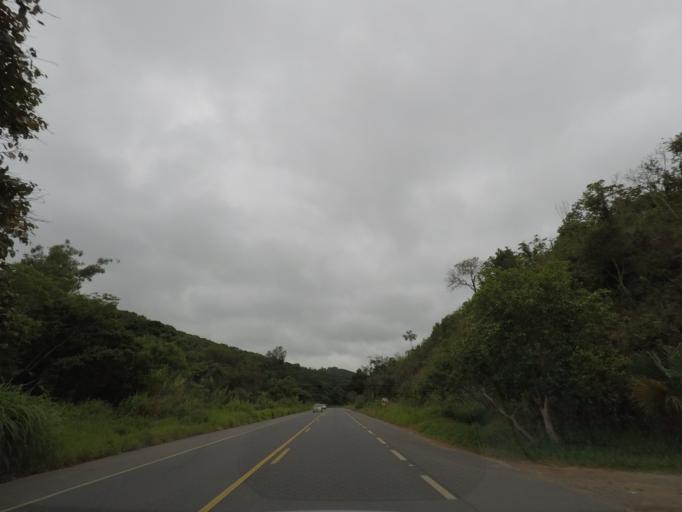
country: BR
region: Sao Paulo
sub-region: Cunha
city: Cunha
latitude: -22.9522
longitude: -45.0546
